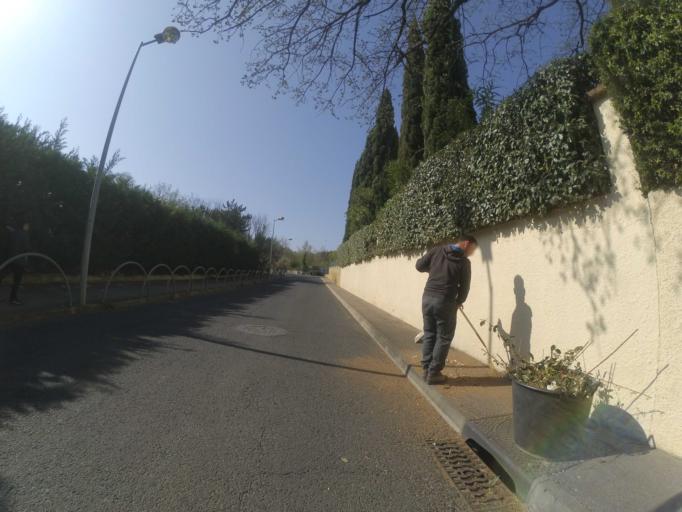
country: FR
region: Languedoc-Roussillon
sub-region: Departement des Pyrenees-Orientales
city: Thuir
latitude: 42.6269
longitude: 2.7511
